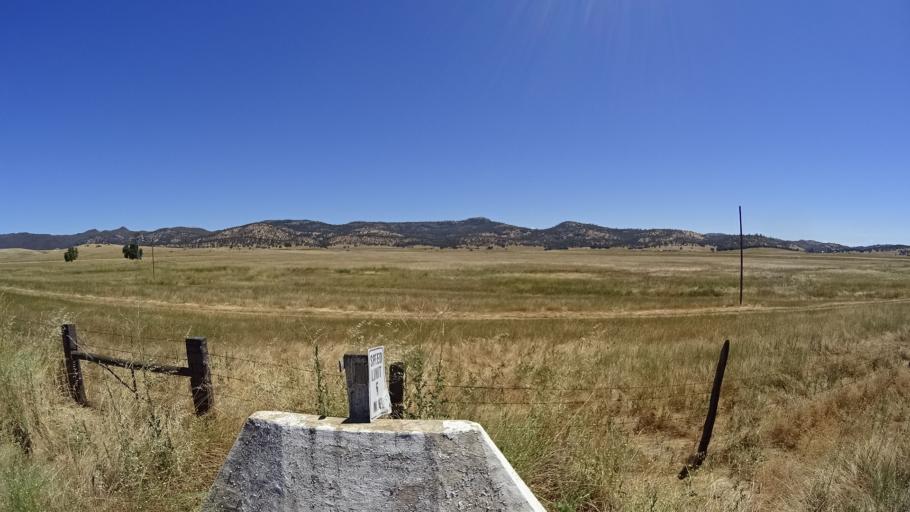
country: US
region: California
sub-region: Calaveras County
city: Copperopolis
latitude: 38.0339
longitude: -120.7201
